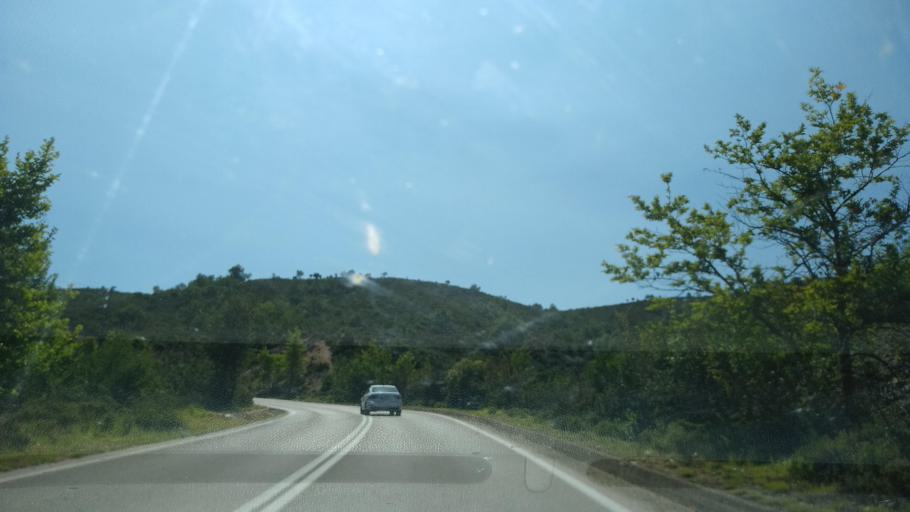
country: GR
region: Central Macedonia
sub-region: Nomos Chalkidikis
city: Arnaia
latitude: 40.5001
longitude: 23.5083
